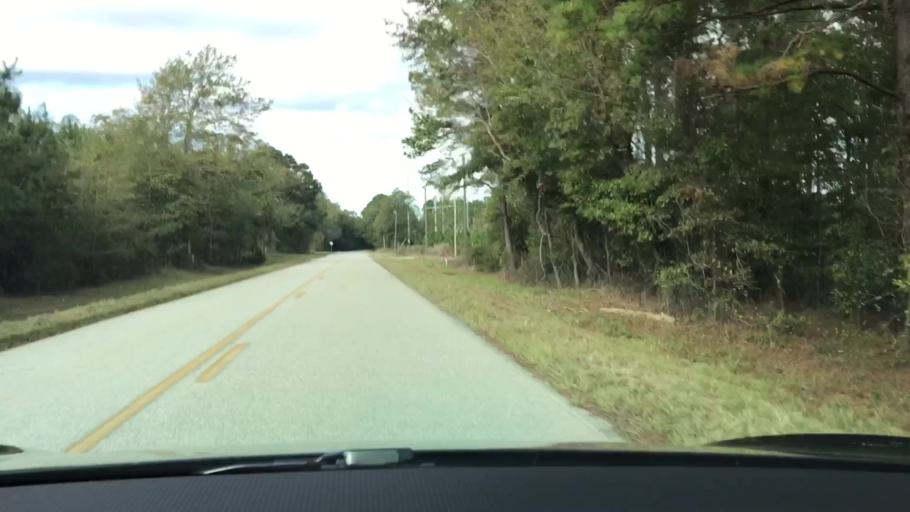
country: US
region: Georgia
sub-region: Jefferson County
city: Wadley
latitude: 32.8076
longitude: -82.3946
